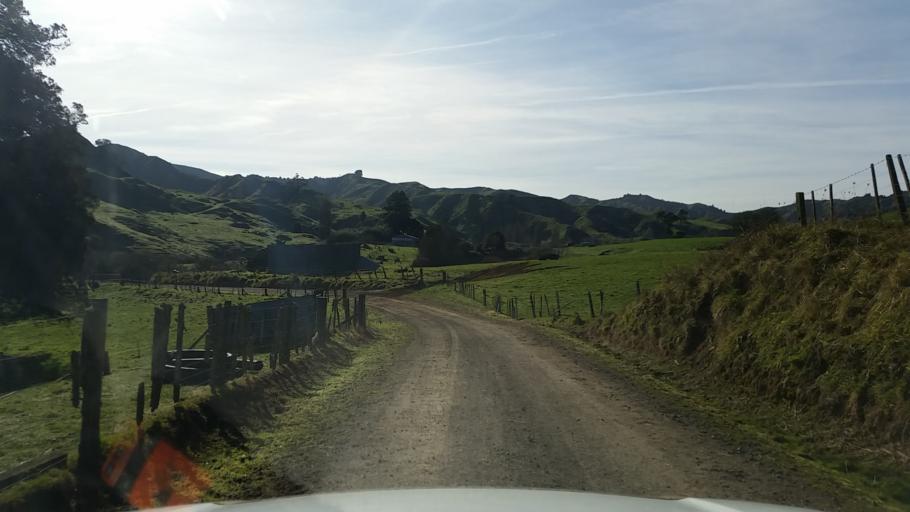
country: NZ
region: Taranaki
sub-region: South Taranaki District
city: Eltham
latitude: -39.3125
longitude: 174.5370
